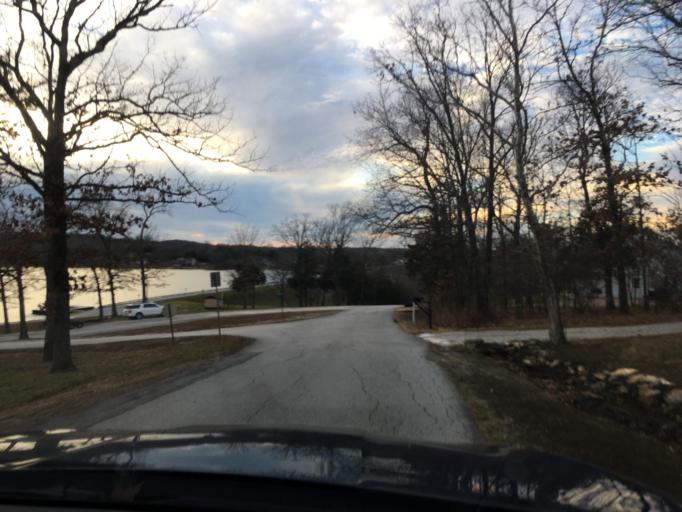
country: US
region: Missouri
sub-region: Jefferson County
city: De Soto
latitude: 38.0955
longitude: -90.5678
